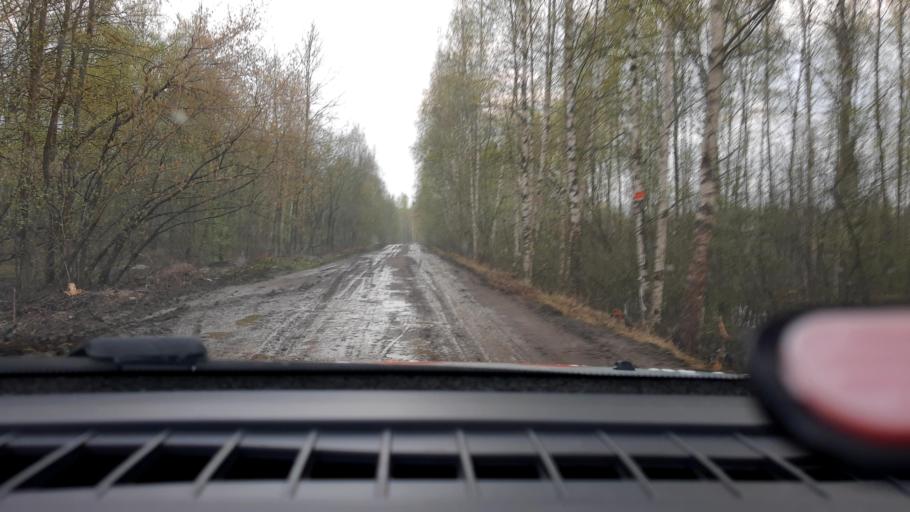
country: RU
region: Nizjnij Novgorod
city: Gorbatovka
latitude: 56.3009
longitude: 43.7699
